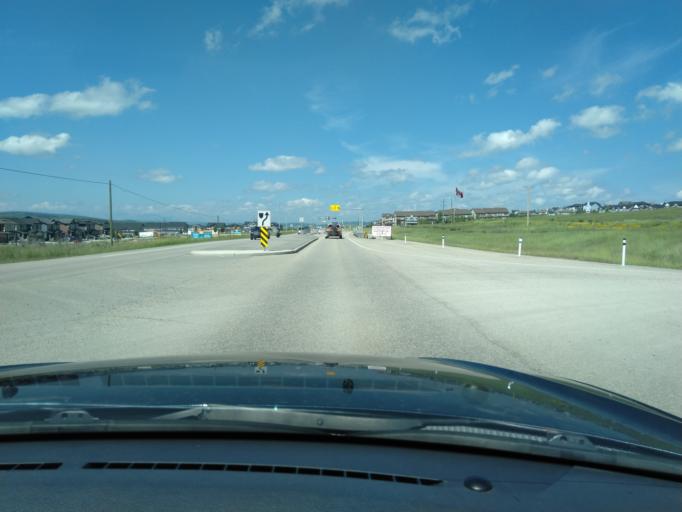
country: CA
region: Alberta
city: Cochrane
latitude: 51.2027
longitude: -114.5005
